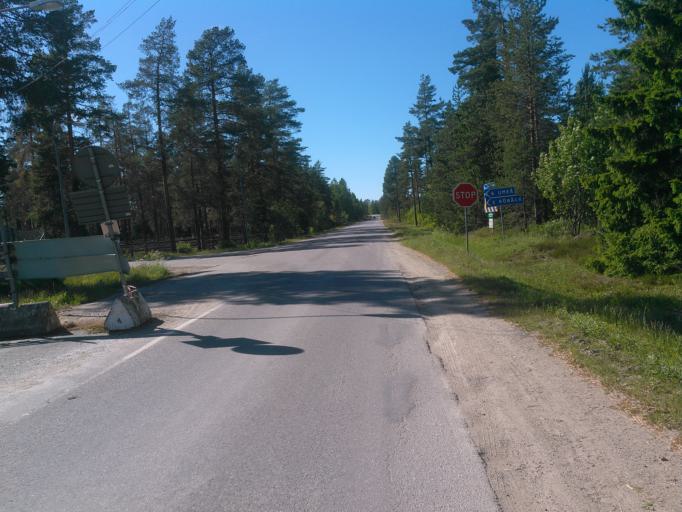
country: SE
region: Vaesterbotten
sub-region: Umea Kommun
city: Roback
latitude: 63.8243
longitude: 20.1780
